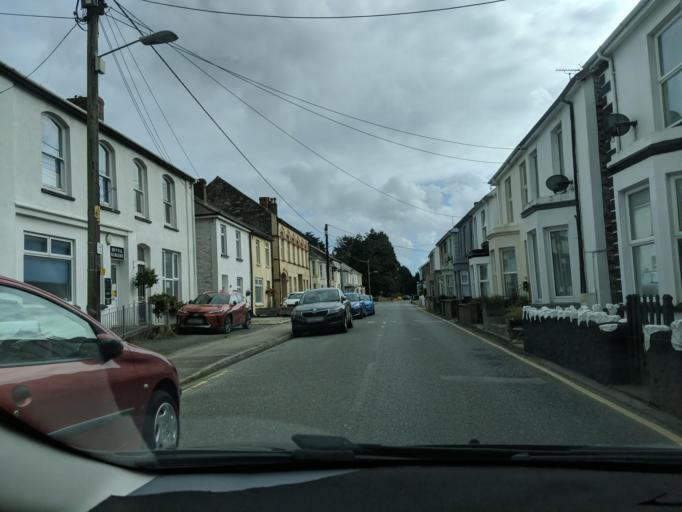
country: GB
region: England
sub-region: Cornwall
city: Par
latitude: 50.3589
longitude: -4.7136
